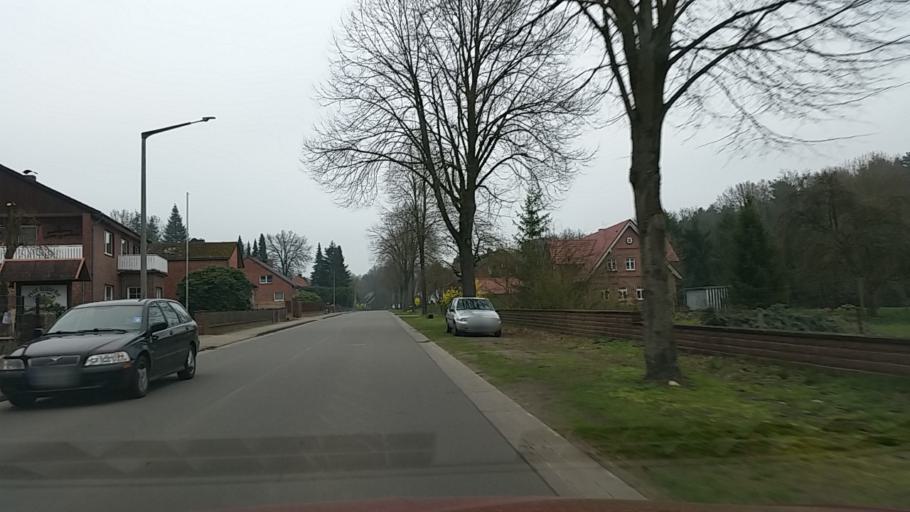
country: DE
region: Lower Saxony
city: Hankensbuttel
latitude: 52.6799
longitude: 10.5750
